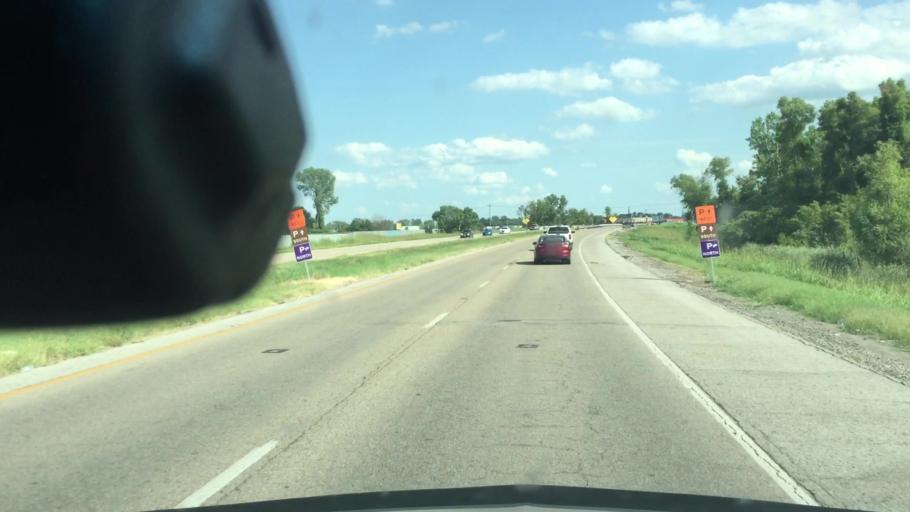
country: US
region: Illinois
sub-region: Madison County
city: Madison
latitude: 38.6590
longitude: -90.1368
